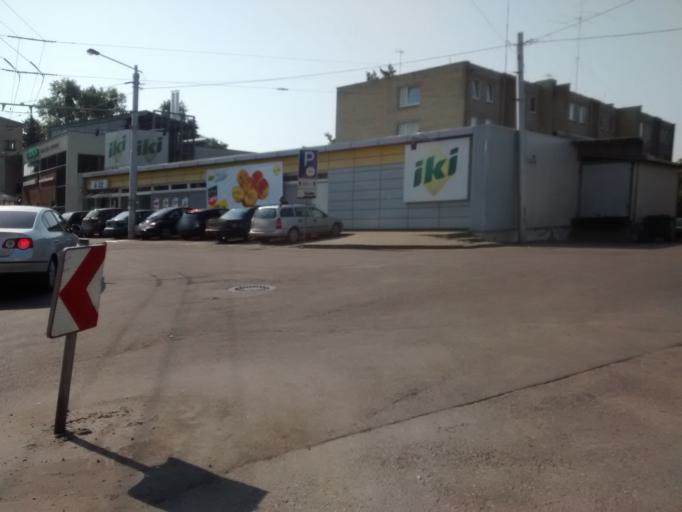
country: LT
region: Kauno apskritis
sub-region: Kaunas
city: Eiguliai
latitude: 54.9144
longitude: 23.9206
